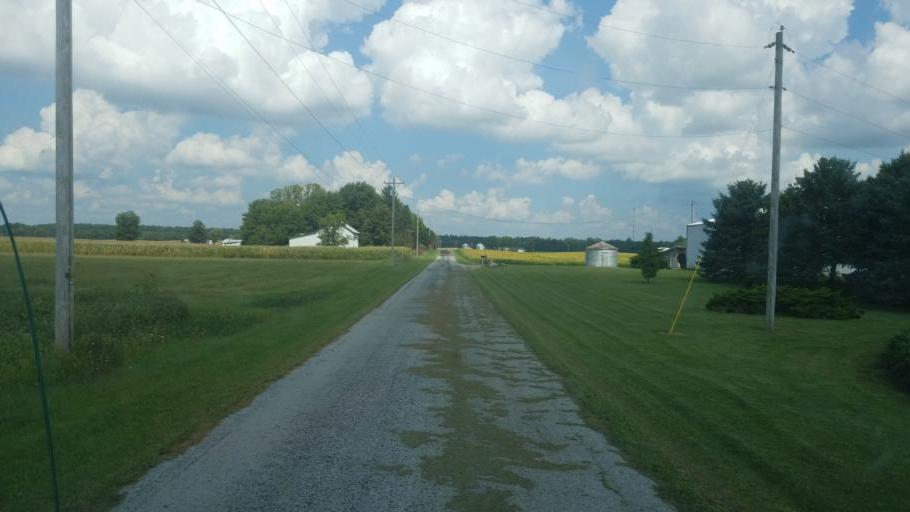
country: US
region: Ohio
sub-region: Hardin County
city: Kenton
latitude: 40.6978
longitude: -83.6386
